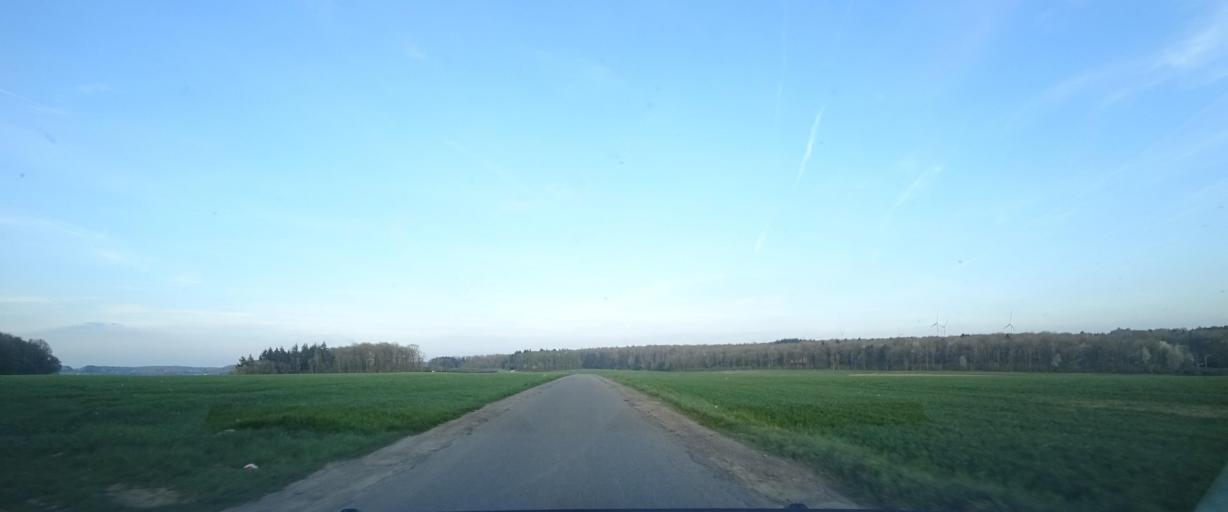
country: BE
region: Wallonia
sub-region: Province de Namur
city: Hamois
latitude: 50.3093
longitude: 5.1580
